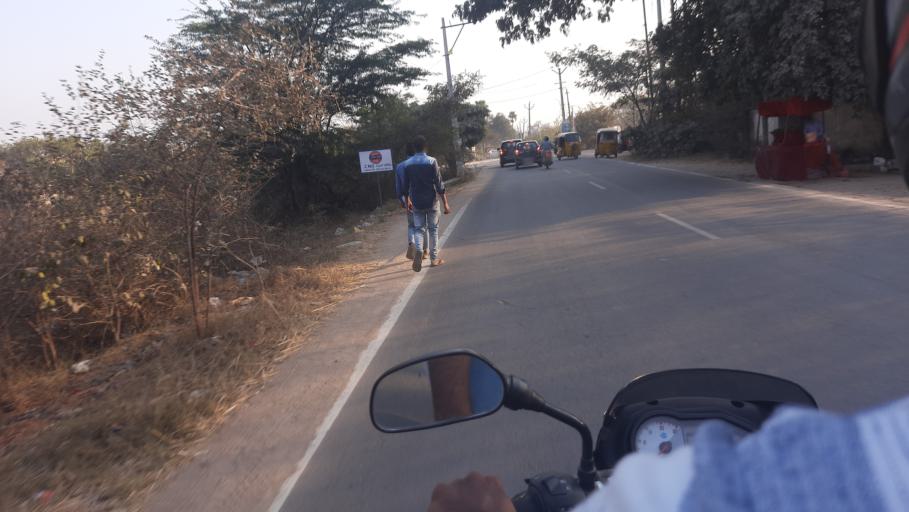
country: IN
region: Telangana
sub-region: Rangareddi
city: Secunderabad
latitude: 17.5136
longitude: 78.5401
